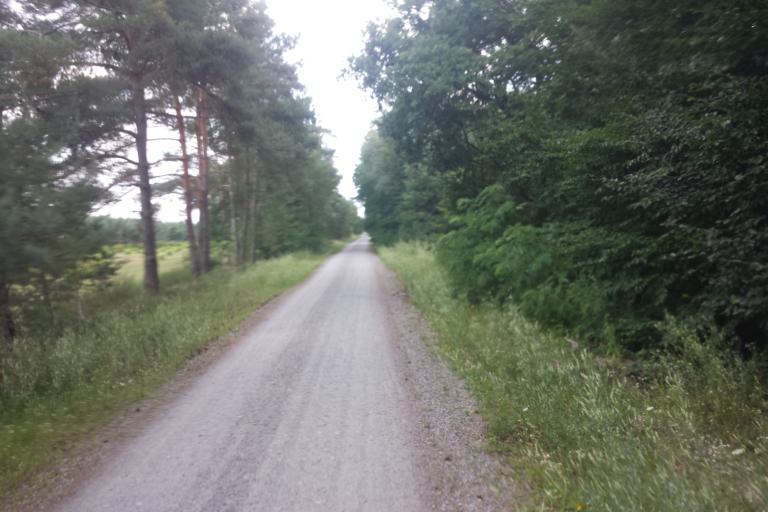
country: DE
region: Hesse
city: Viernheim
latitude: 49.5661
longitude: 8.5279
